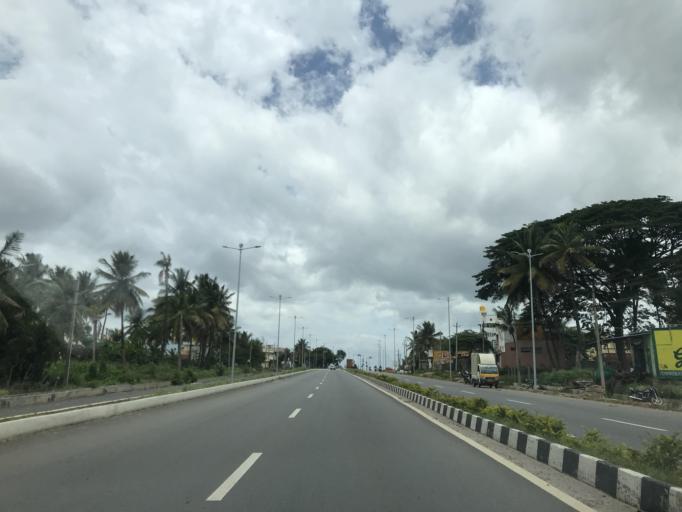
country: IN
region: Karnataka
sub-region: Tumkur
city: Tumkur
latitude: 13.3084
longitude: 77.1455
